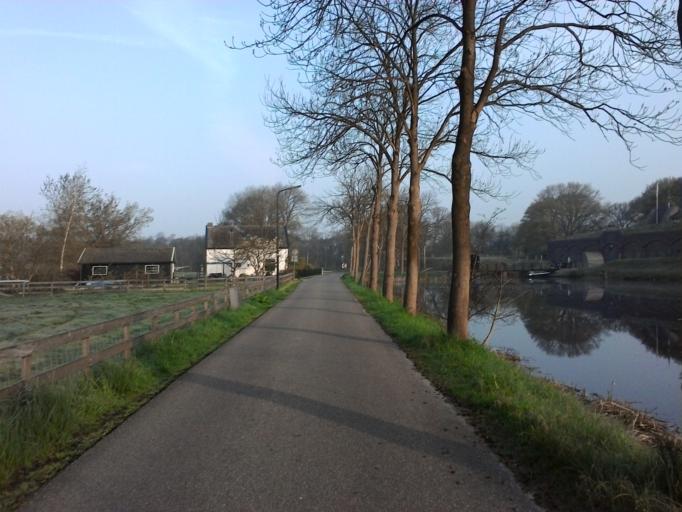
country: NL
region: Utrecht
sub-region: Gemeente Utrecht
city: Utrecht
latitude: 52.1278
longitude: 5.1300
